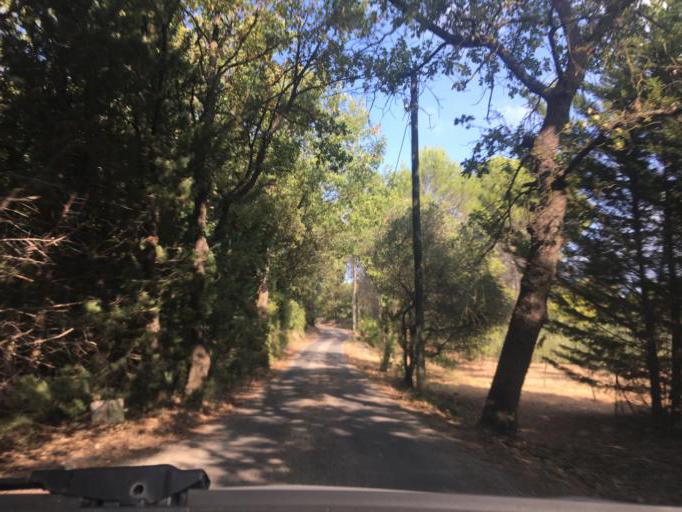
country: FR
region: Provence-Alpes-Cote d'Azur
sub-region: Departement du Var
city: Lorgues
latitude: 43.4912
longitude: 6.3959
